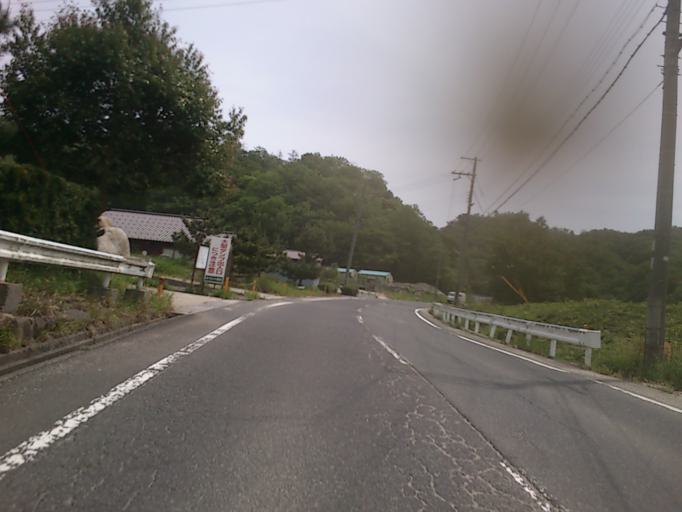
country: JP
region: Kyoto
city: Miyazu
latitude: 35.5878
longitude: 135.1116
